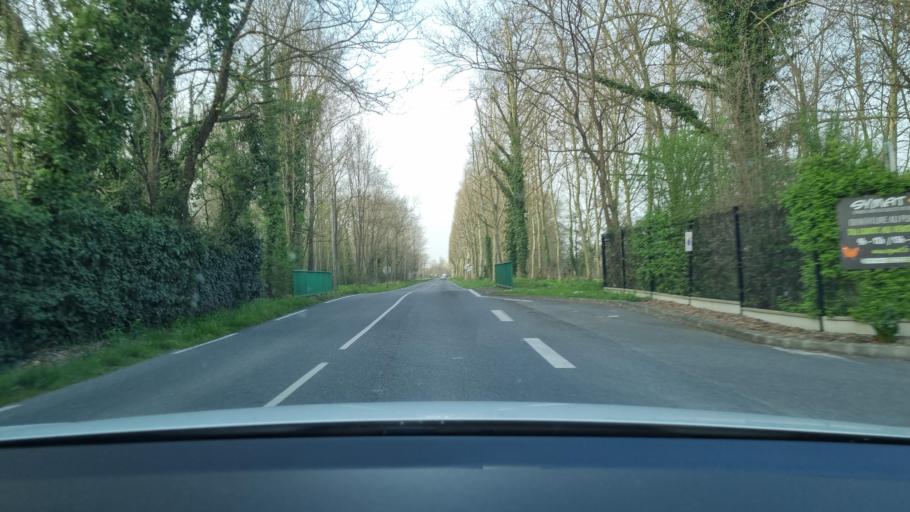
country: FR
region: Midi-Pyrenees
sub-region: Departement des Hautes-Pyrenees
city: Bazet
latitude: 43.2722
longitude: 0.0800
